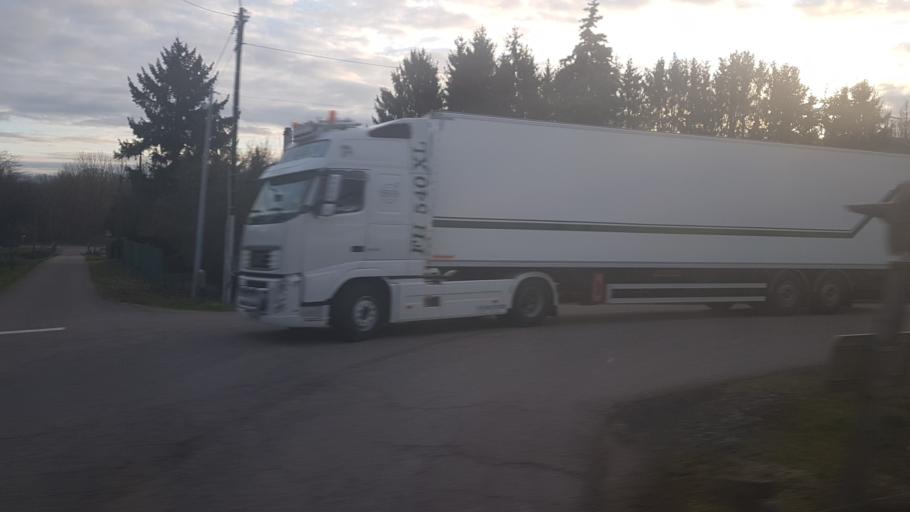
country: FR
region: Lorraine
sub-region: Departement des Vosges
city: Igney
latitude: 48.2833
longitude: 6.3980
